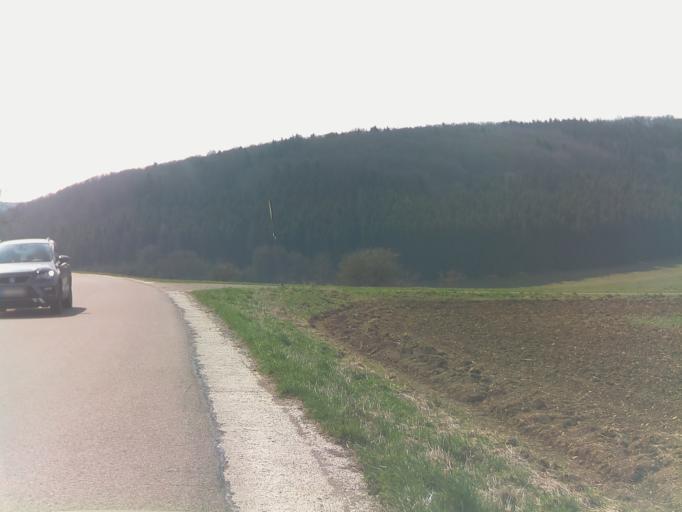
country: DE
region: Baden-Wuerttemberg
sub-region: Tuebingen Region
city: Bad Urach
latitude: 48.4508
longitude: 9.4064
